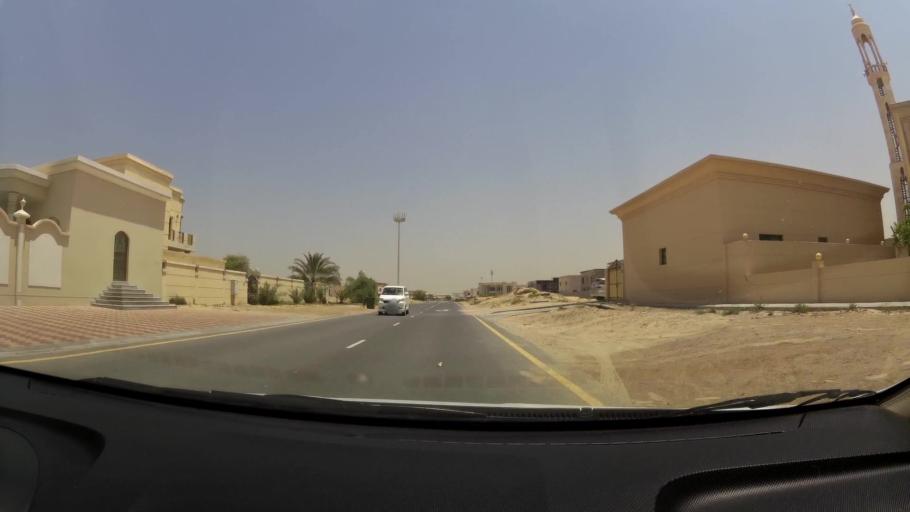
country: AE
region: Ajman
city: Ajman
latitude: 25.4051
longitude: 55.5229
